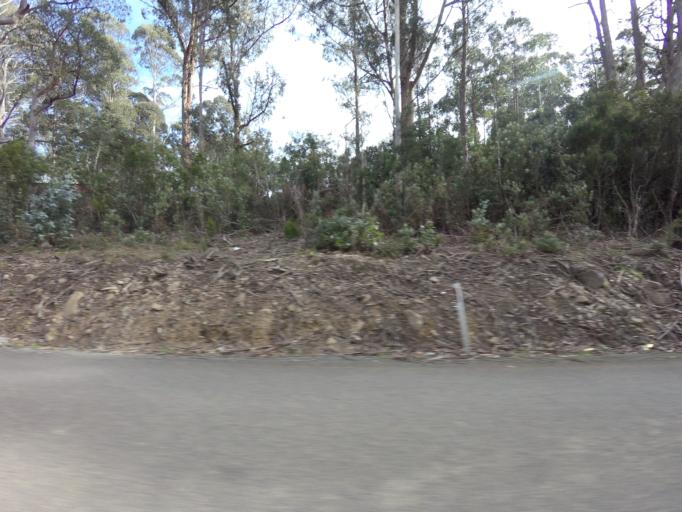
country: AU
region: Tasmania
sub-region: Kingborough
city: Margate
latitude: -42.9870
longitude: 147.1925
